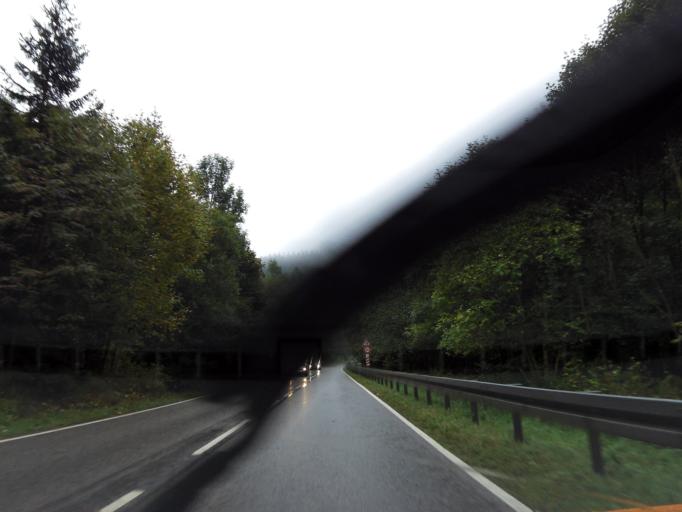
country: DE
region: Thuringia
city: Ilfeld
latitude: 51.6265
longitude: 10.8180
